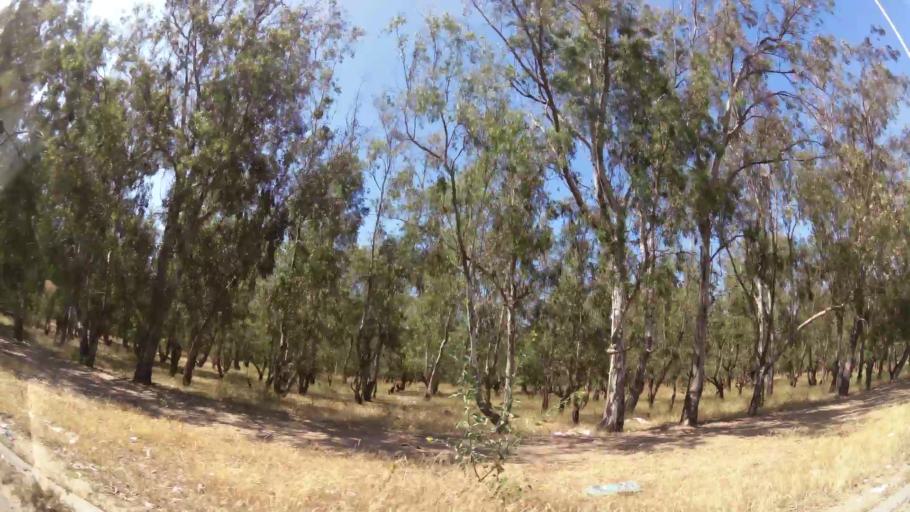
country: MA
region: Gharb-Chrarda-Beni Hssen
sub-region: Kenitra Province
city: Kenitra
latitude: 34.2370
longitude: -6.5600
